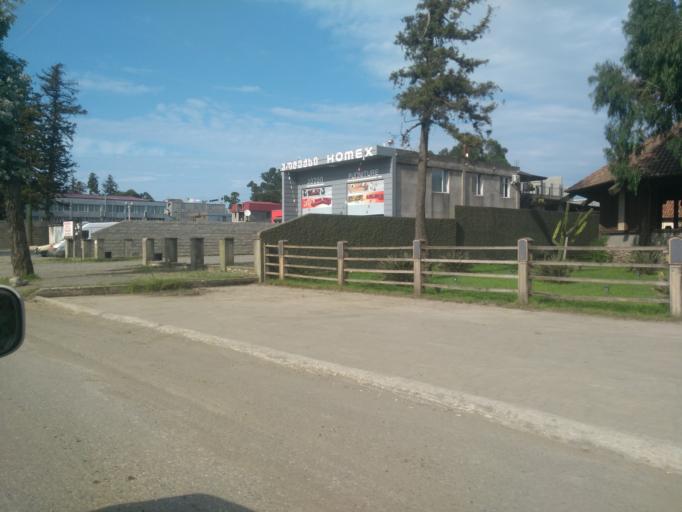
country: GE
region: Ajaria
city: Batumi
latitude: 41.6102
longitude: 41.6253
